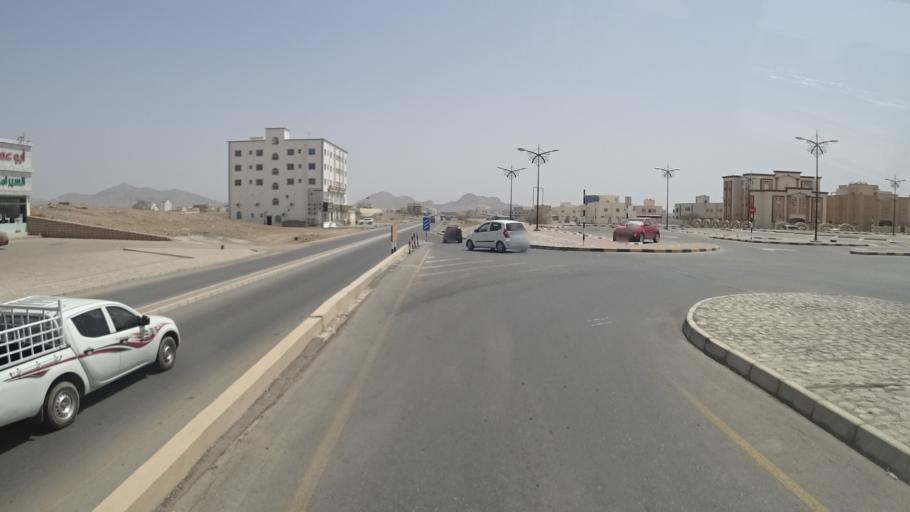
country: OM
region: Muhafazat ad Dakhiliyah
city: Nizwa
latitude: 22.8756
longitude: 57.5399
